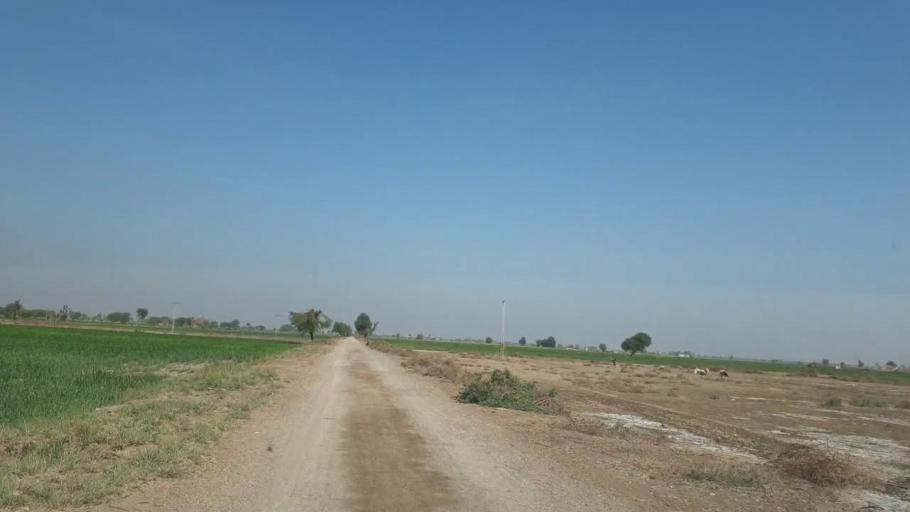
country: PK
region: Sindh
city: Mirpur Khas
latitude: 25.5603
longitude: 69.1837
